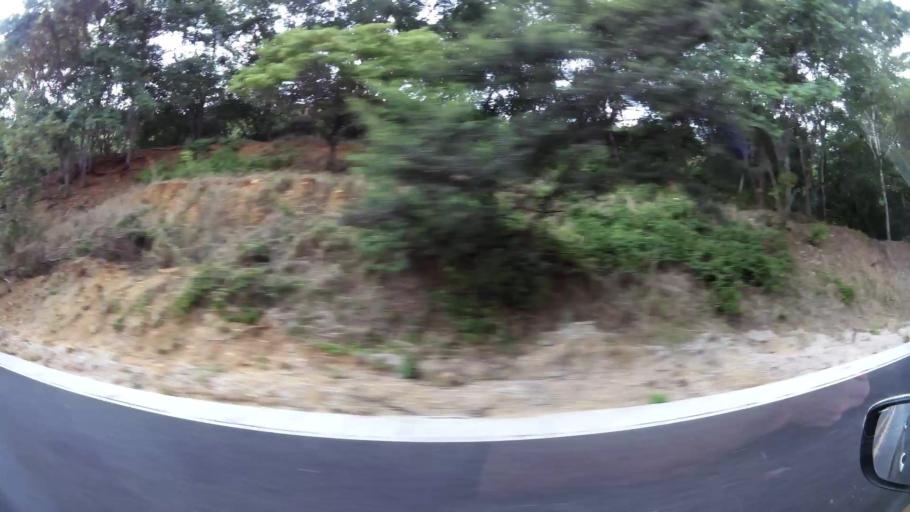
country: CR
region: Guanacaste
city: Nandayure
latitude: 10.2217
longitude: -85.2130
